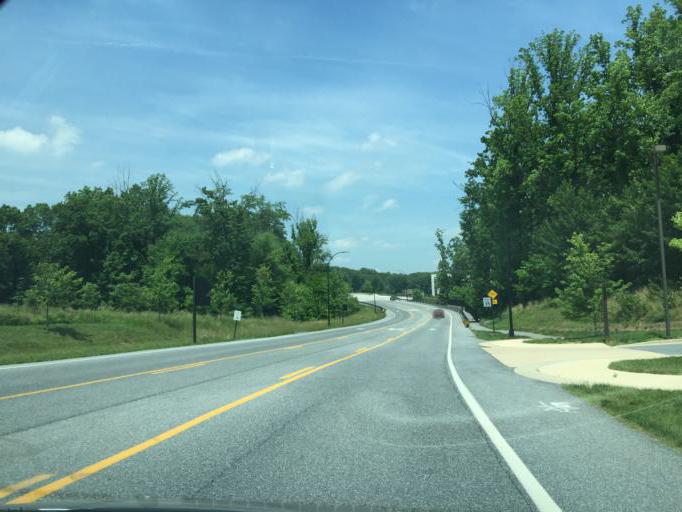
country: US
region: Maryland
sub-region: Howard County
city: Hanover
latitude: 39.1896
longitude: -76.6998
